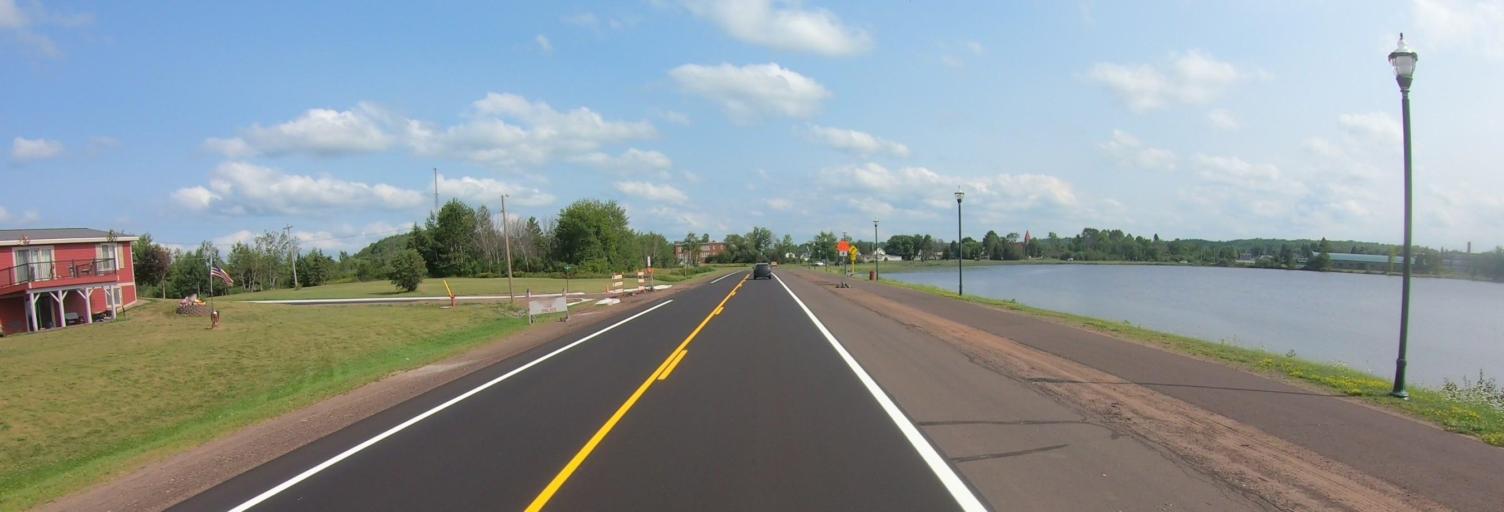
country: US
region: Michigan
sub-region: Gogebic County
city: Wakefield
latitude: 46.4834
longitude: -89.9352
